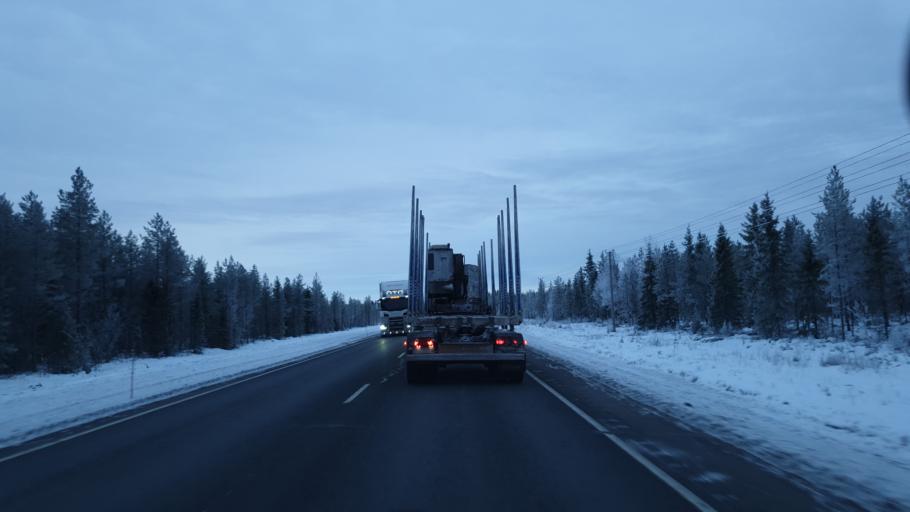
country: FI
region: Northern Ostrobothnia
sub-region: Oulunkaari
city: Ii
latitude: 65.3823
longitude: 25.3778
